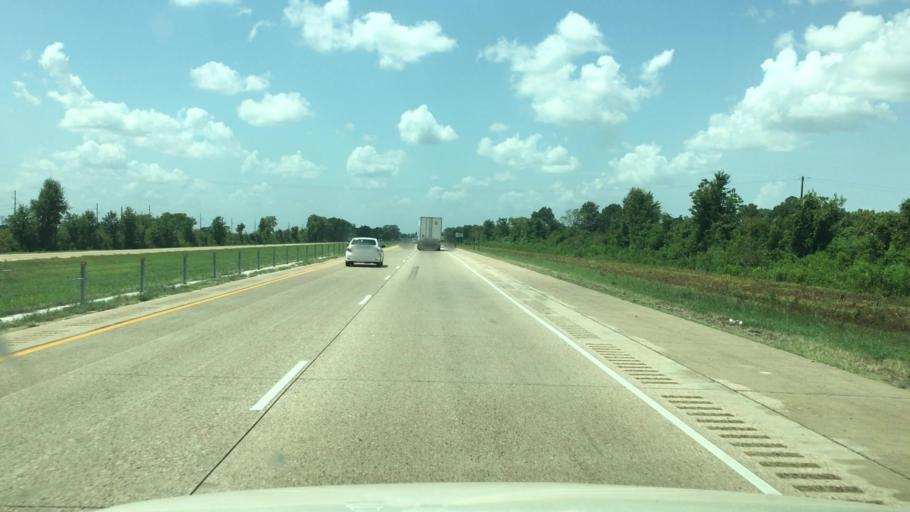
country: US
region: Arkansas
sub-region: Miller County
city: Texarkana
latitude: 33.5643
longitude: -93.8567
